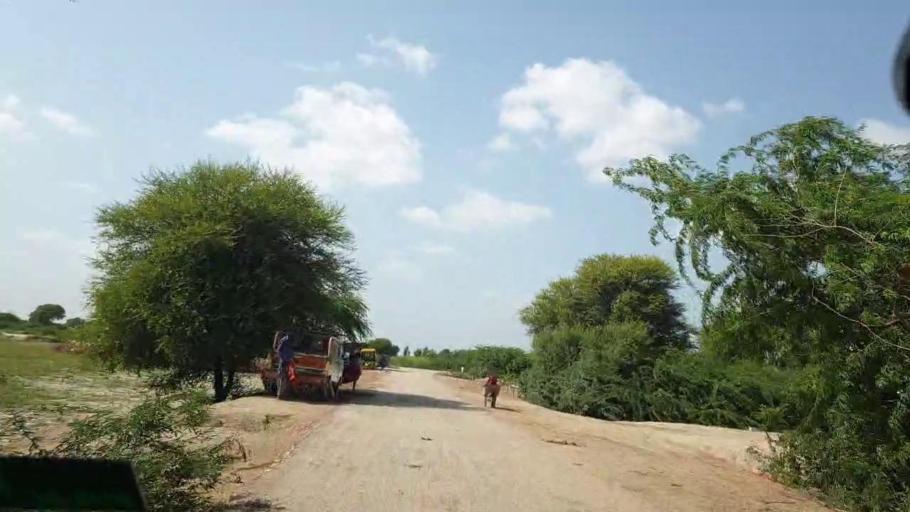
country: PK
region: Sindh
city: Naukot
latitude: 24.6501
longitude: 69.2196
